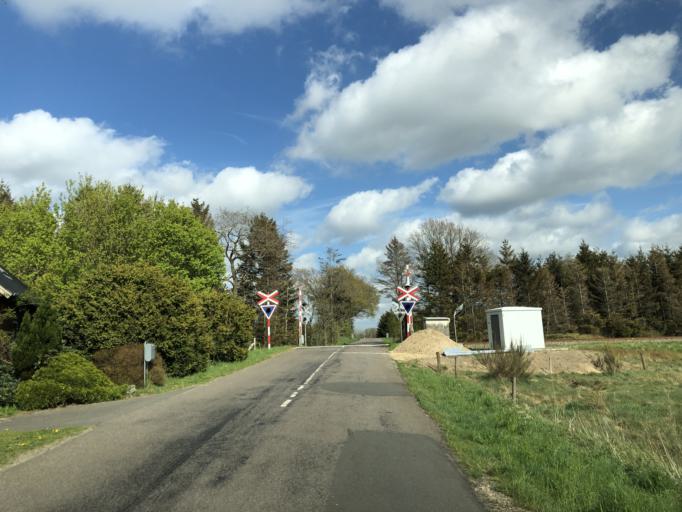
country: DK
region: Central Jutland
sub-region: Herning Kommune
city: Avlum
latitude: 56.3050
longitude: 8.7332
